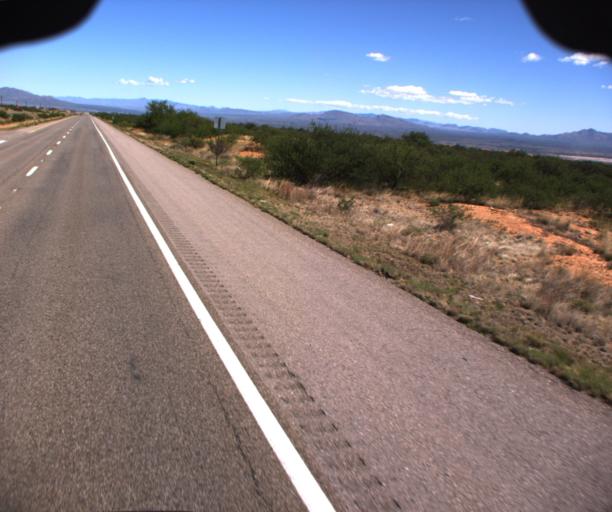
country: US
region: Arizona
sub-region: Cochise County
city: Whetstone
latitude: 31.9135
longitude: -110.3410
